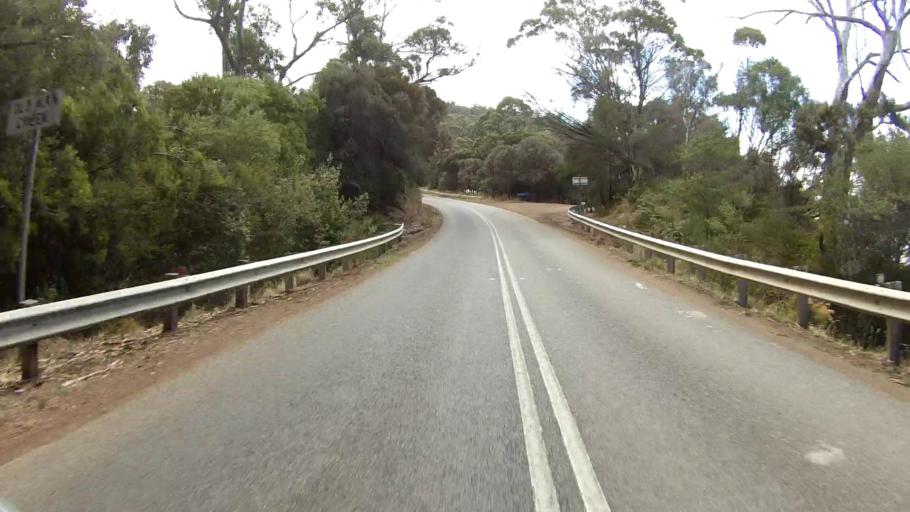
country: AU
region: Tasmania
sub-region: Sorell
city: Sorell
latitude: -42.2410
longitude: 148.0123
